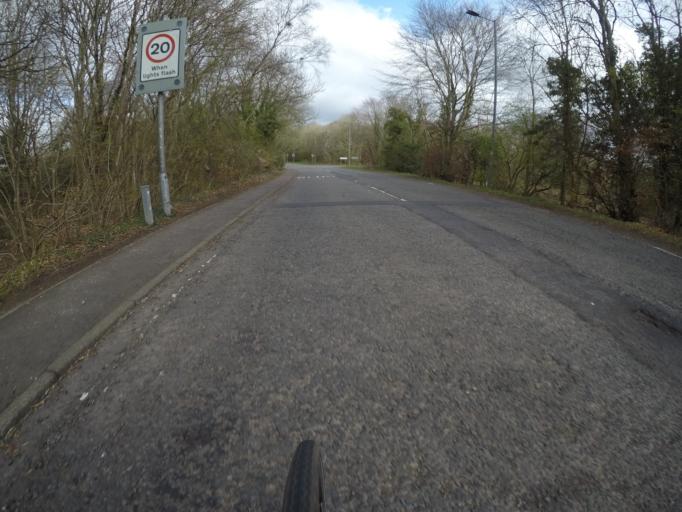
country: GB
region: Scotland
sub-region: North Ayrshire
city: Irvine
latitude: 55.6335
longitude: -4.6334
